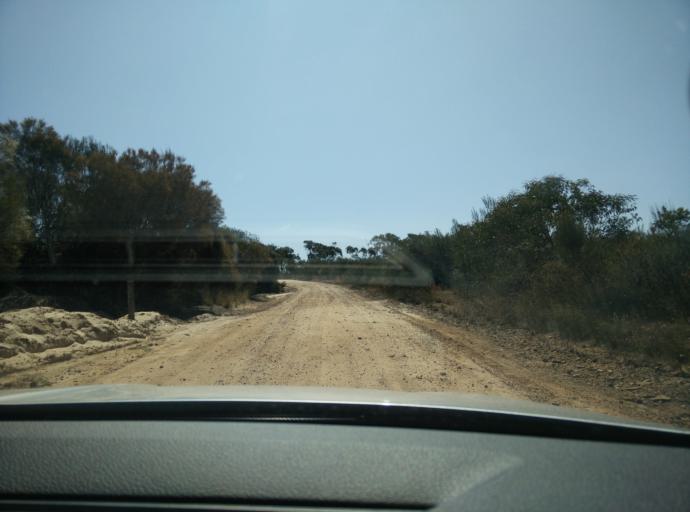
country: AU
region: New South Wales
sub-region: Gosford Shire
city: Umina
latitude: -33.5471
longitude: 151.2863
